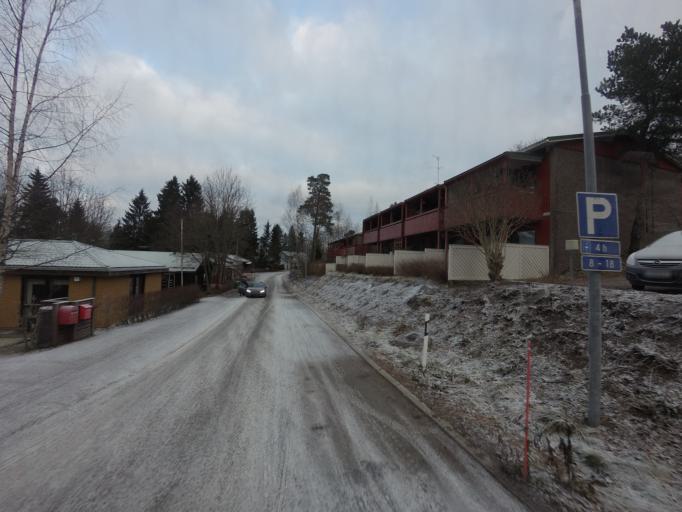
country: FI
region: Uusimaa
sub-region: Helsinki
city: Espoo
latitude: 60.1983
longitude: 24.6794
